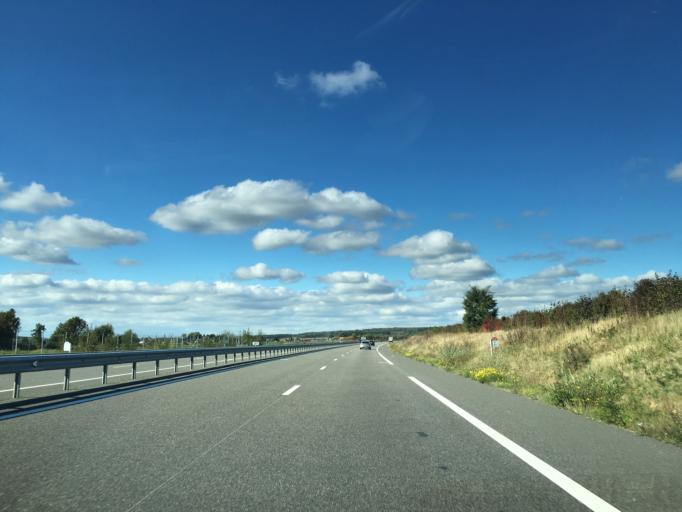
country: FR
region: Lorraine
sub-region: Departement de Meurthe-et-Moselle
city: Baccarat
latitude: 48.4798
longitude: 6.7150
